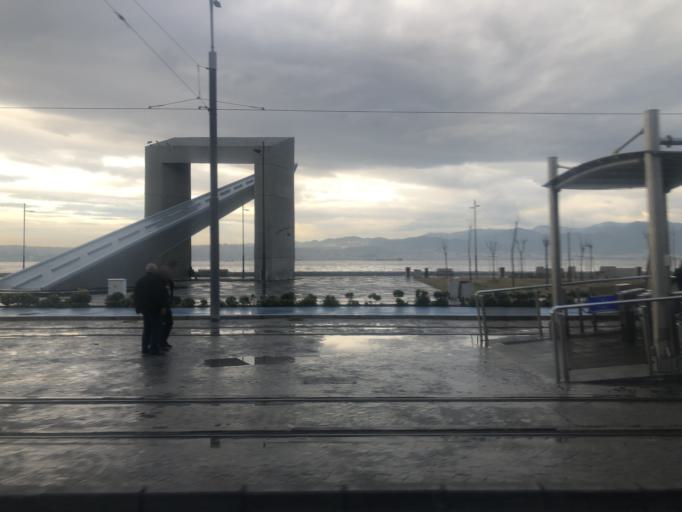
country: TR
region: Izmir
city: Karsiyaka
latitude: 38.4497
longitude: 27.1107
